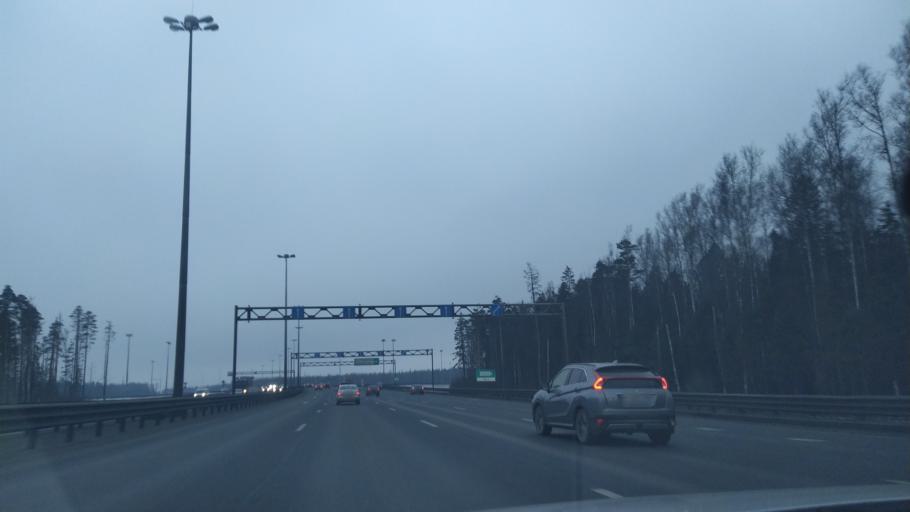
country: RU
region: St.-Petersburg
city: Krasnogvargeisky
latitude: 59.9507
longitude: 30.5446
